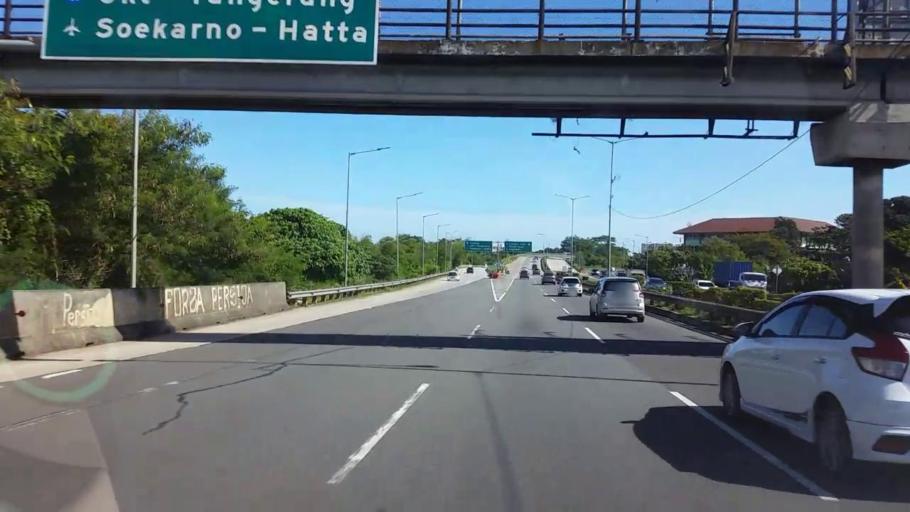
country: ID
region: Banten
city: South Tangerang
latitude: -6.2544
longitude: 106.7610
